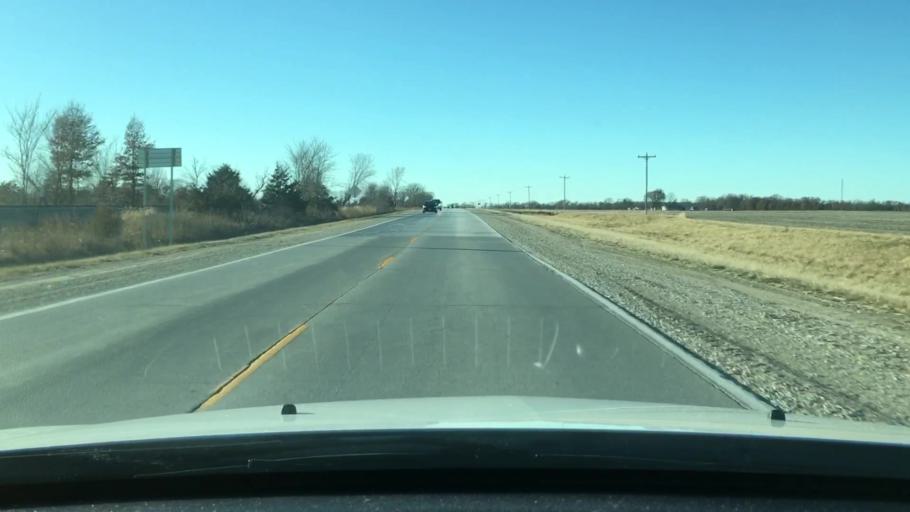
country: US
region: Missouri
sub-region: Boone County
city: Centralia
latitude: 39.1922
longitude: -92.0121
